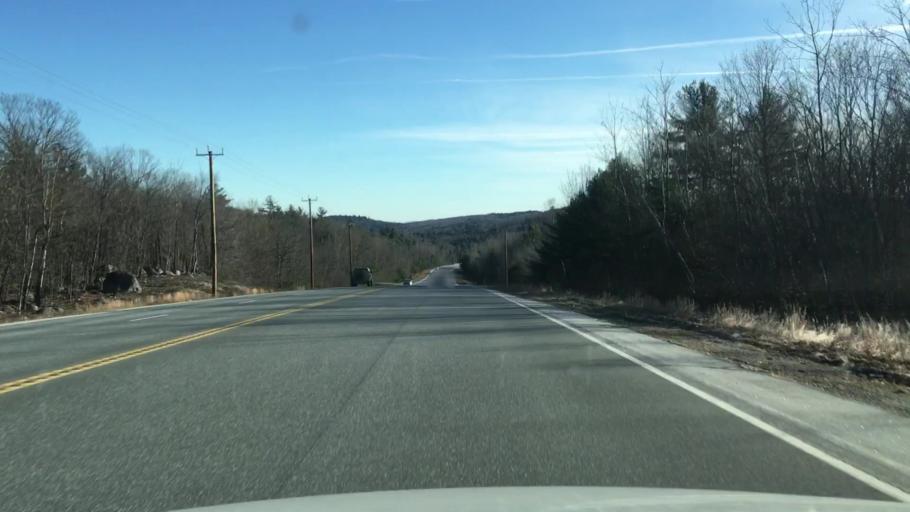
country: US
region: Maine
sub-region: Hancock County
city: Dedham
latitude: 44.6878
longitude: -68.5839
